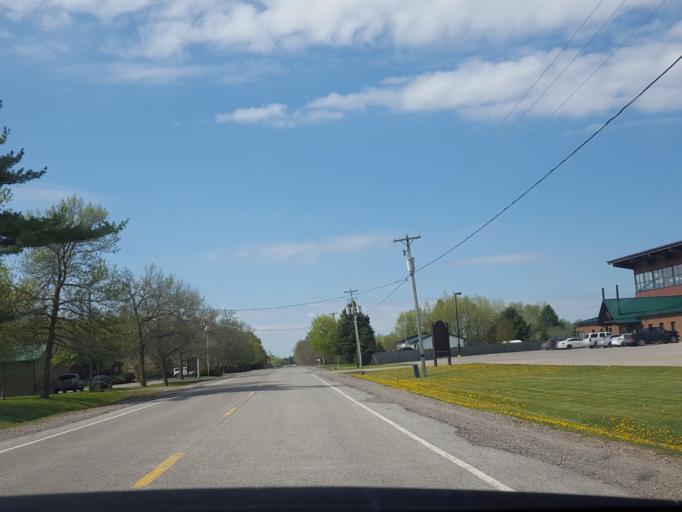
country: CA
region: Ontario
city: Uxbridge
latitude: 44.1952
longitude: -78.8802
